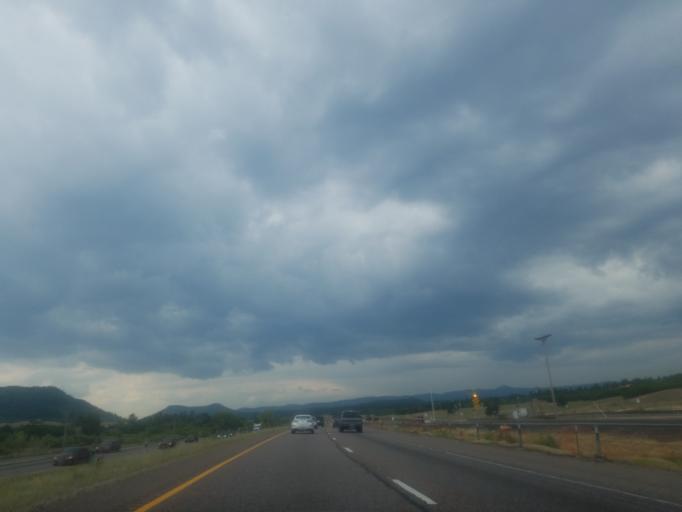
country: US
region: Colorado
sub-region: Douglas County
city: Castle Rock
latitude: 39.2985
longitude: -104.8907
